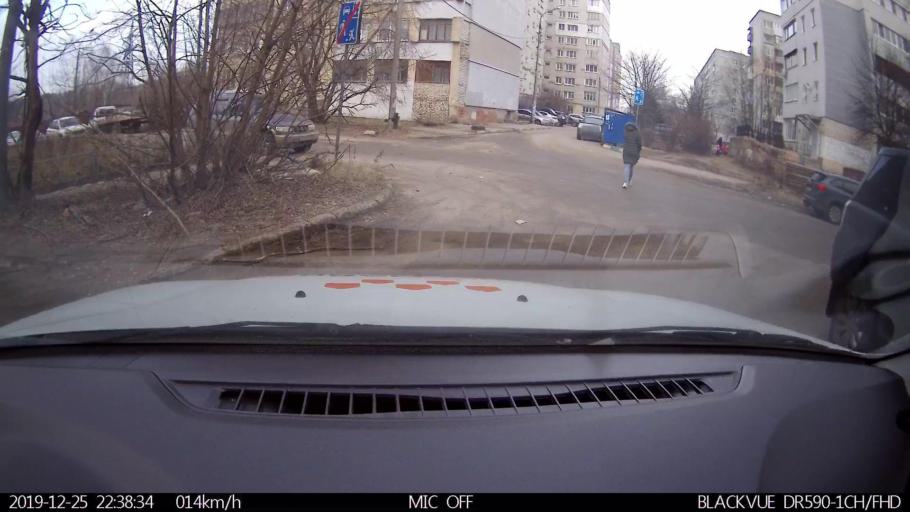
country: RU
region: Nizjnij Novgorod
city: Nizhniy Novgorod
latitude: 56.3367
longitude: 43.8718
